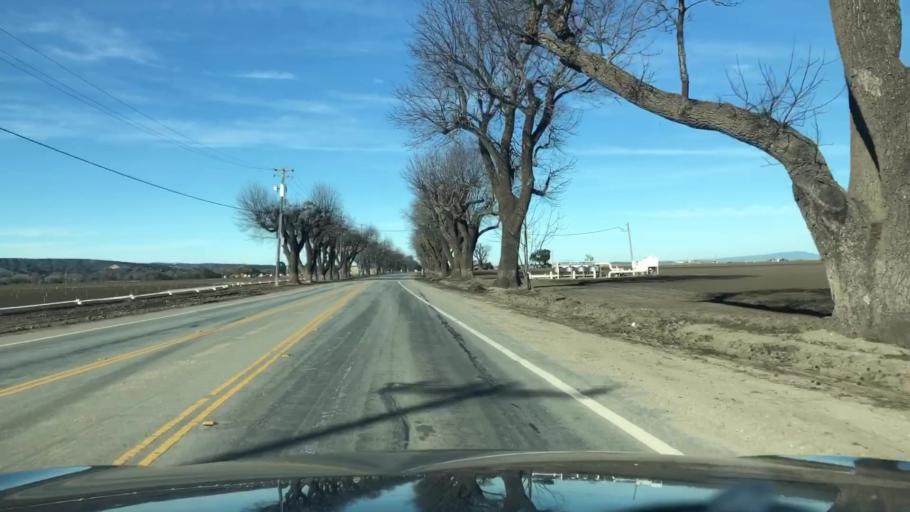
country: US
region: California
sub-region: Monterey County
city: Salinas
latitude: 36.6244
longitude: -121.6525
